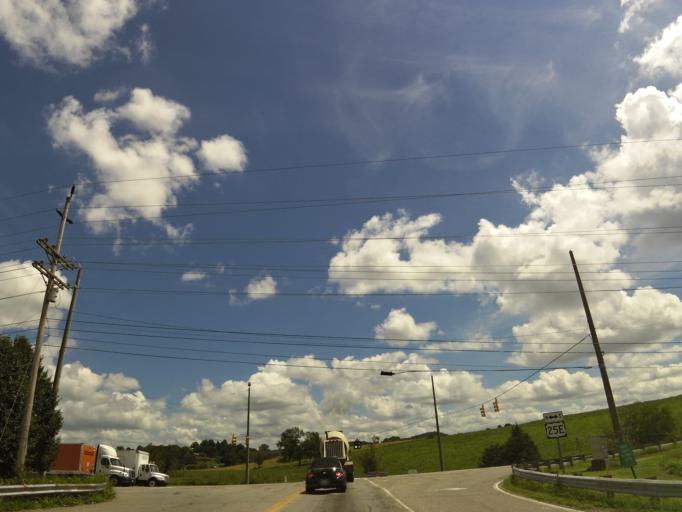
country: US
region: Tennessee
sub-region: Claiborne County
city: Harrogate
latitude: 36.5671
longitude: -83.6541
